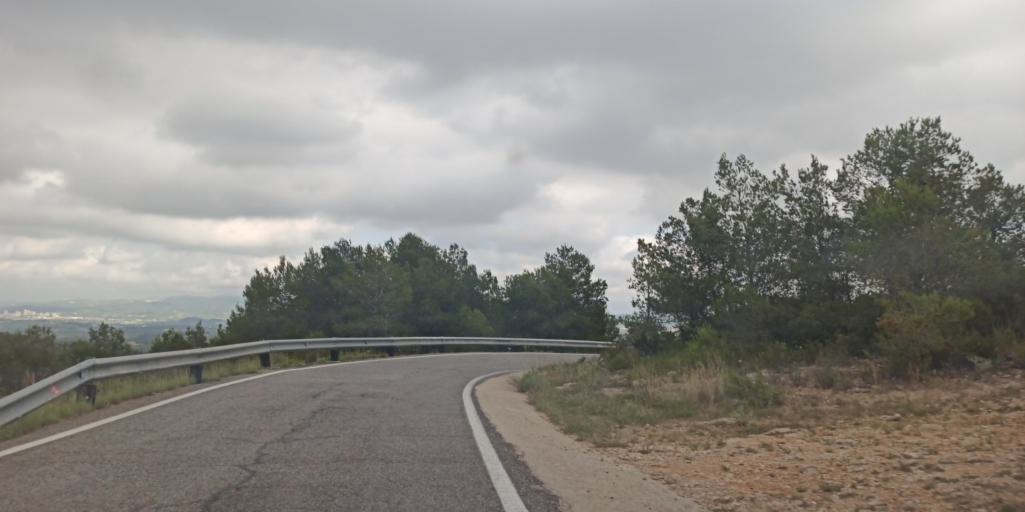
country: ES
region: Catalonia
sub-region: Provincia de Tarragona
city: Sant Jaume dels Domenys
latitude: 41.3237
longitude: 1.5361
